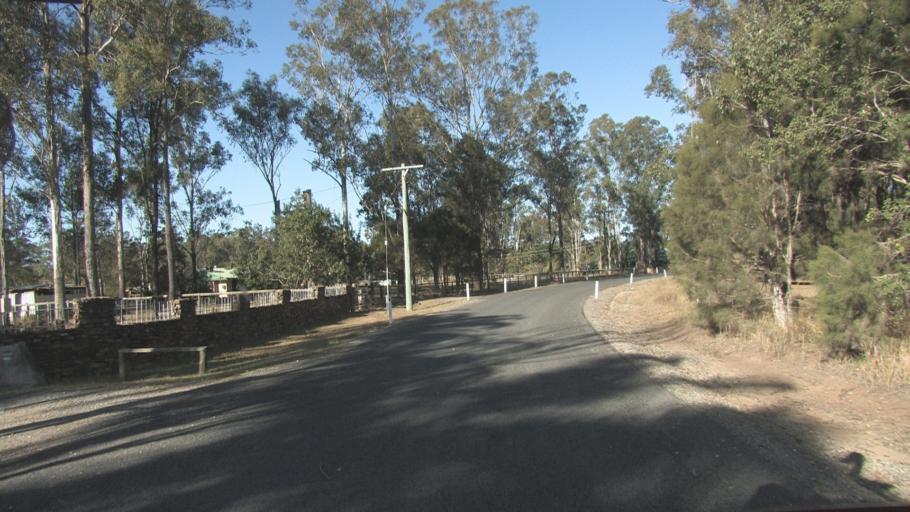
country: AU
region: Queensland
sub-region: Logan
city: Cedar Vale
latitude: -27.8415
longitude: 153.0025
